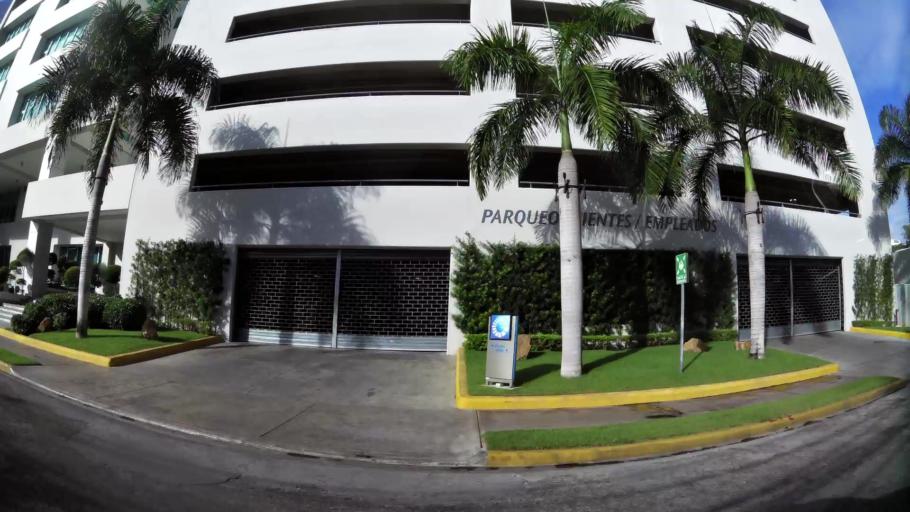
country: DO
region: Nacional
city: La Julia
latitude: 18.4654
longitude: -69.9328
